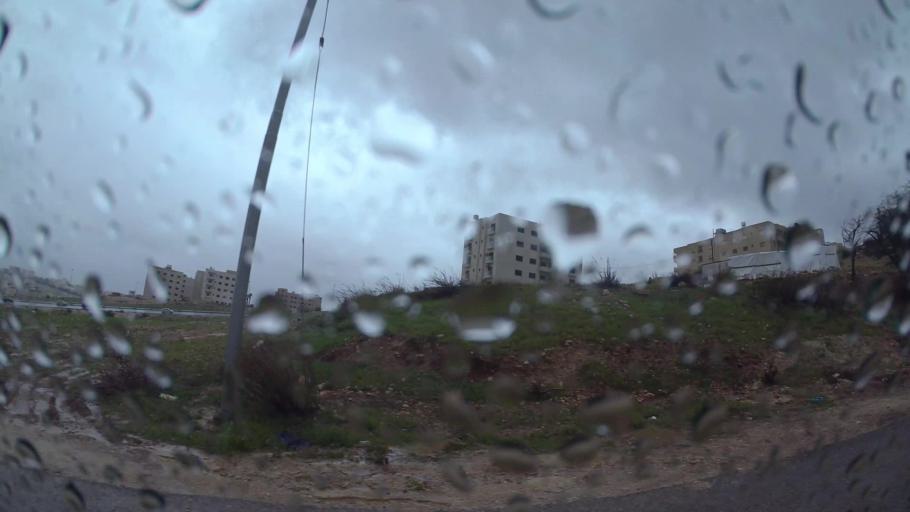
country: JO
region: Amman
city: Al Jubayhah
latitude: 32.0382
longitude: 35.8827
